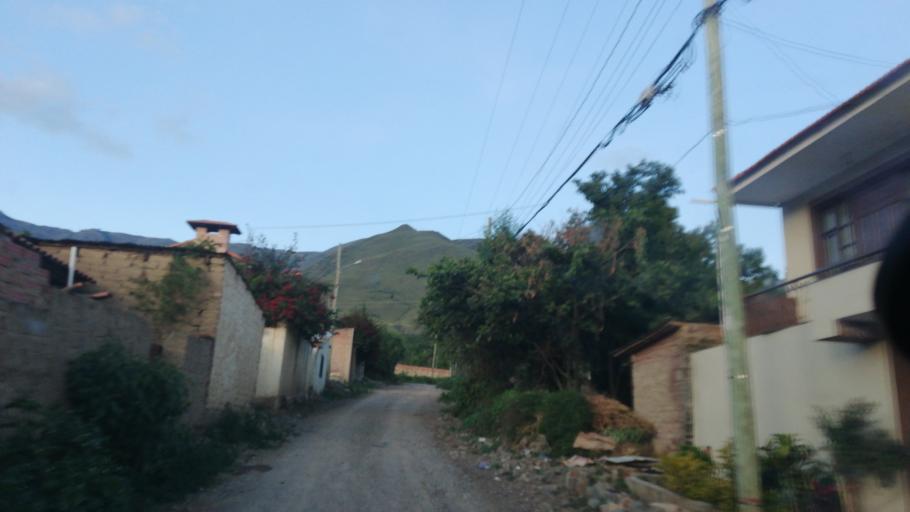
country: BO
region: Cochabamba
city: Cochabamba
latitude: -17.3300
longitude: -66.2058
